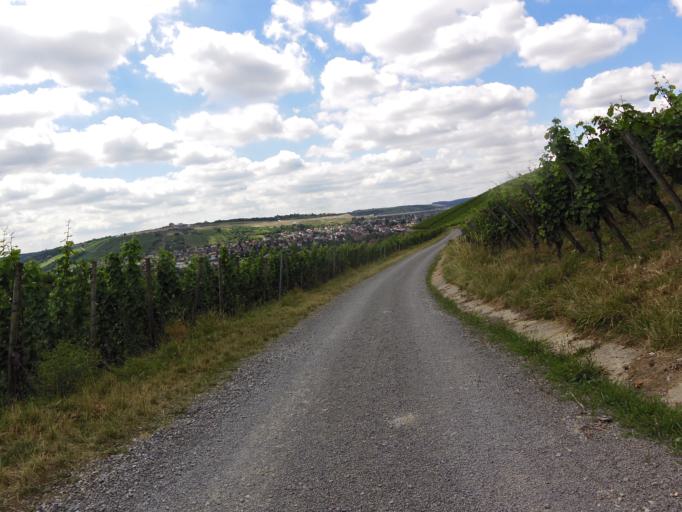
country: DE
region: Bavaria
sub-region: Regierungsbezirk Unterfranken
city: Randersacker
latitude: 49.7718
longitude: 9.9614
